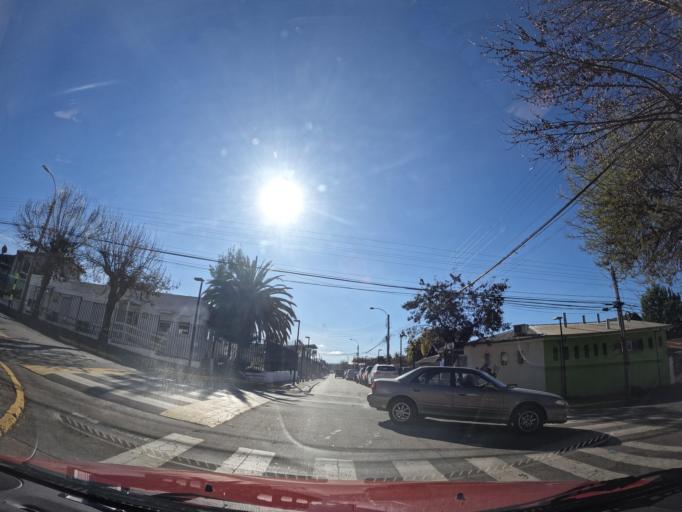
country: CL
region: Maule
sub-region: Provincia de Cauquenes
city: Cauquenes
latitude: -35.9701
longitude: -72.3178
